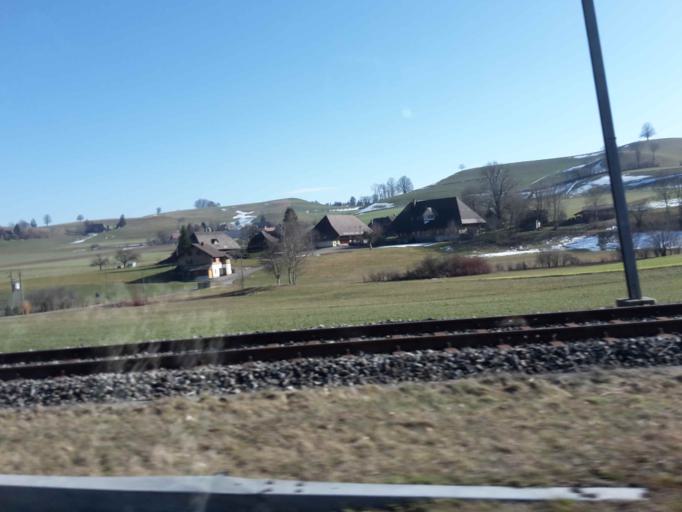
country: CH
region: Bern
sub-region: Emmental District
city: Durrenroth
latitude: 47.0835
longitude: 7.7539
